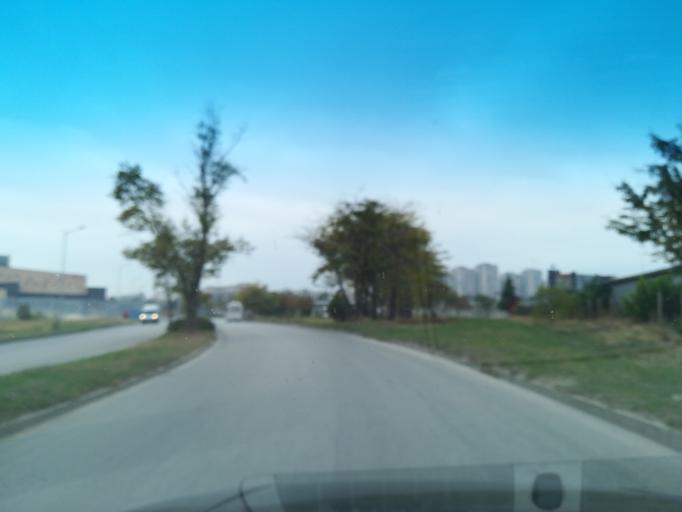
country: BG
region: Plovdiv
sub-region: Obshtina Plovdiv
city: Plovdiv
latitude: 42.1467
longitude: 24.7996
